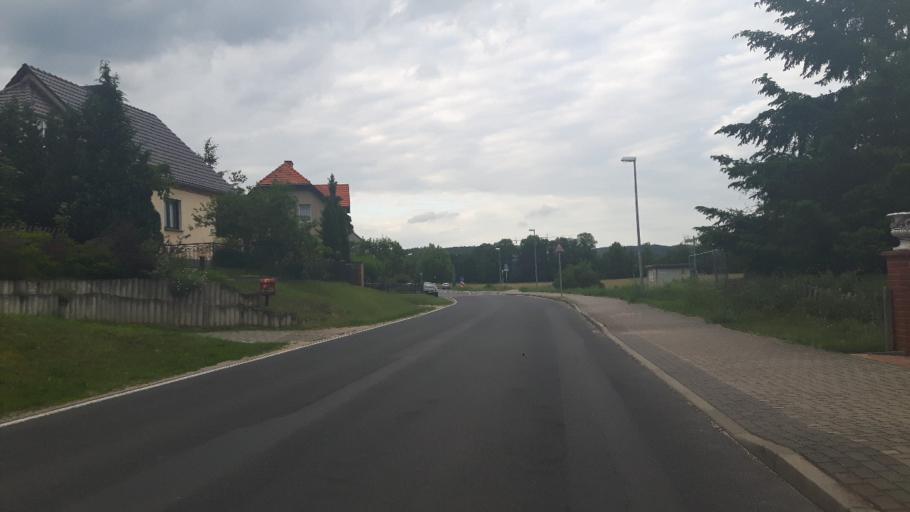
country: DE
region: Brandenburg
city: Niederfinow
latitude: 52.8378
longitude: 13.9369
